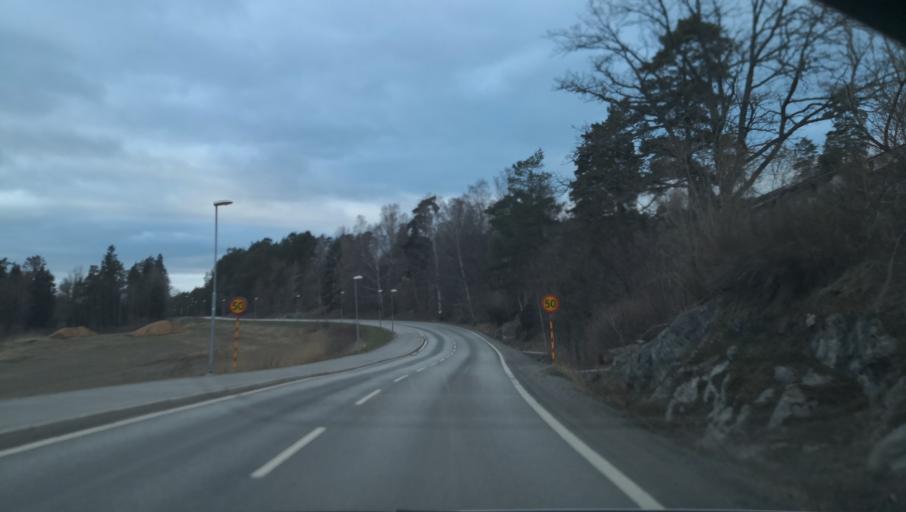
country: SE
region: Stockholm
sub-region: Varmdo Kommun
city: Gustavsberg
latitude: 59.3334
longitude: 18.3863
